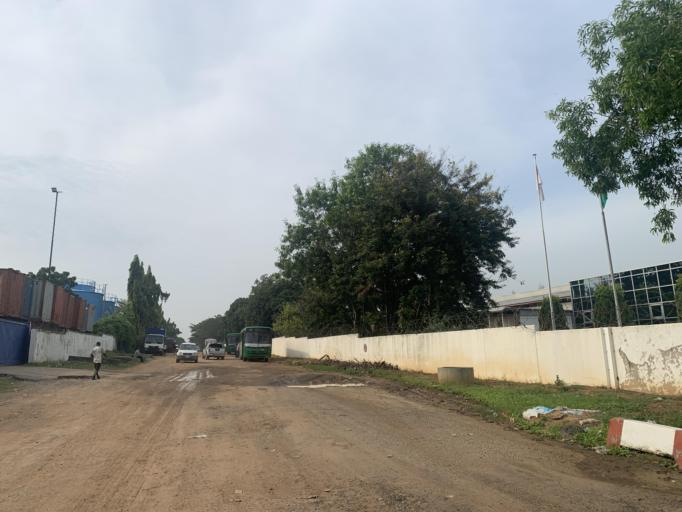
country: NG
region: Abuja Federal Capital Territory
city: Abuja
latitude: 9.0344
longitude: 7.3966
